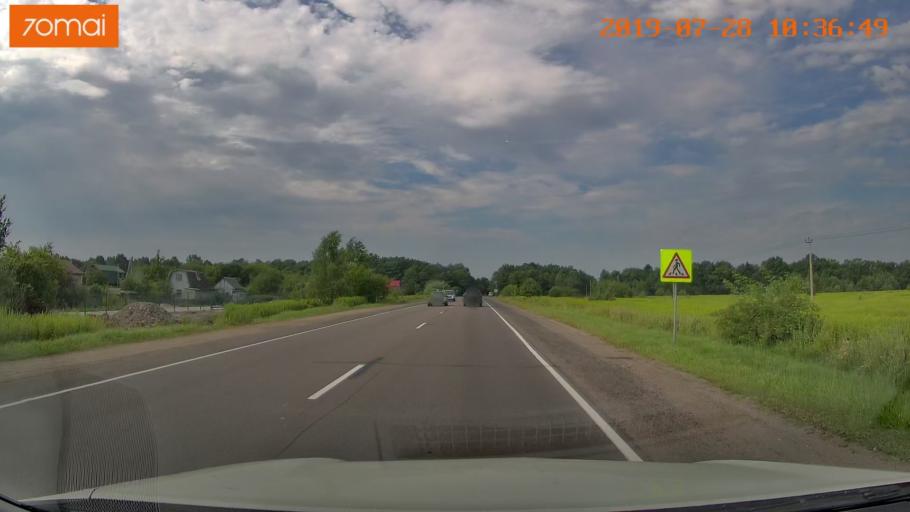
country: RU
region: Kaliningrad
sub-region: Gorod Kaliningrad
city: Kaliningrad
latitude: 54.7355
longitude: 20.4171
